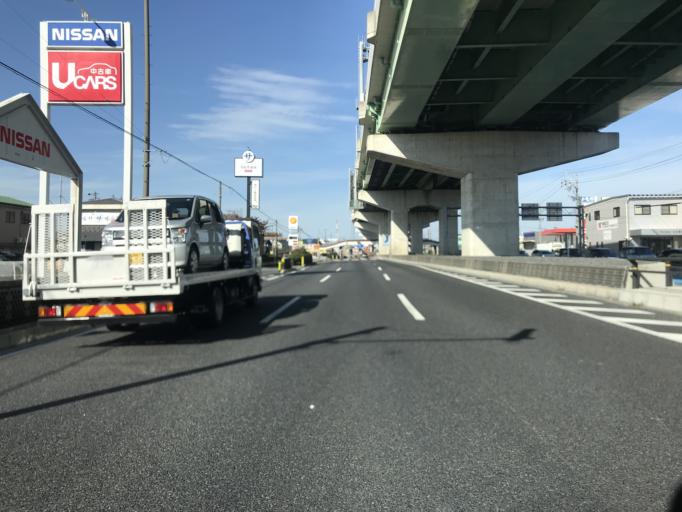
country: JP
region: Aichi
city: Iwakura
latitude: 35.2419
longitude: 136.8465
